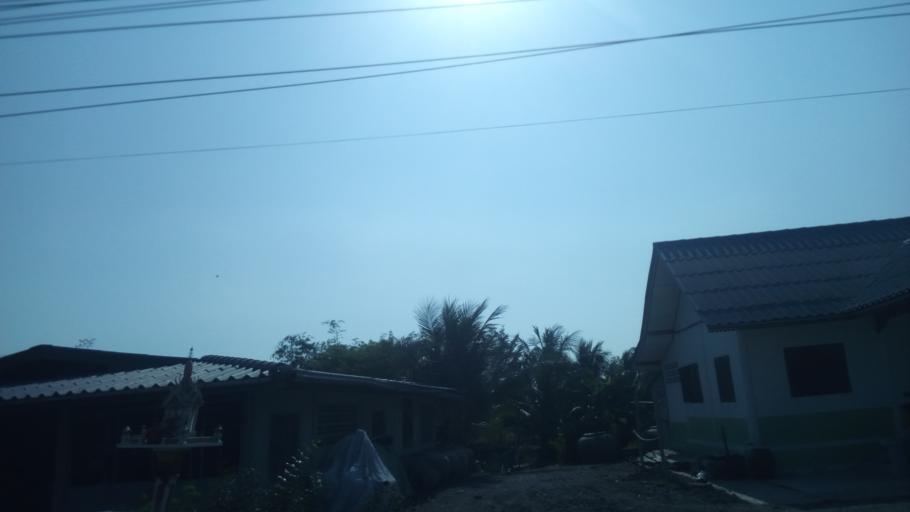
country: TH
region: Nonthaburi
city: Bang Yai
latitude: 13.8994
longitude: 100.3249
